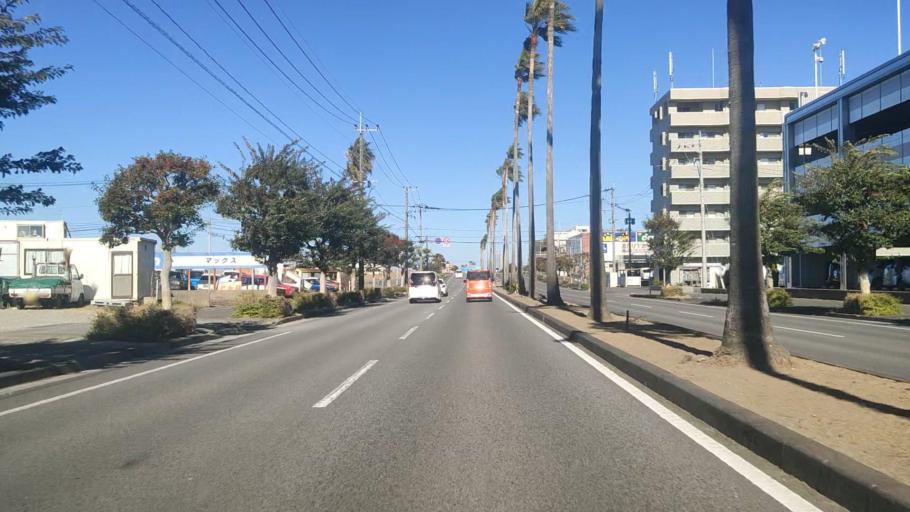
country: JP
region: Miyazaki
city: Miyazaki-shi
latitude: 31.9176
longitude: 131.4502
